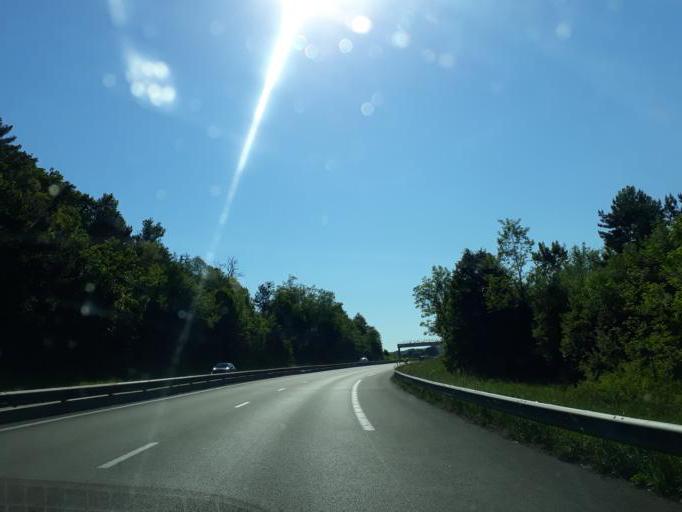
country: FR
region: Bourgogne
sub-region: Departement de la Cote-d'Or
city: Velars-sur-Ouche
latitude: 47.3188
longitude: 4.9264
